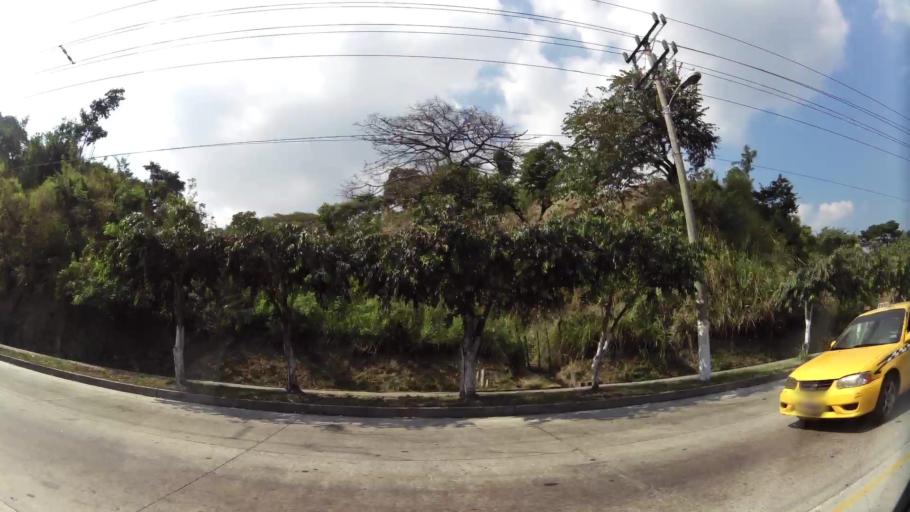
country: SV
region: San Salvador
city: Delgado
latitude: 13.7060
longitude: -89.1711
